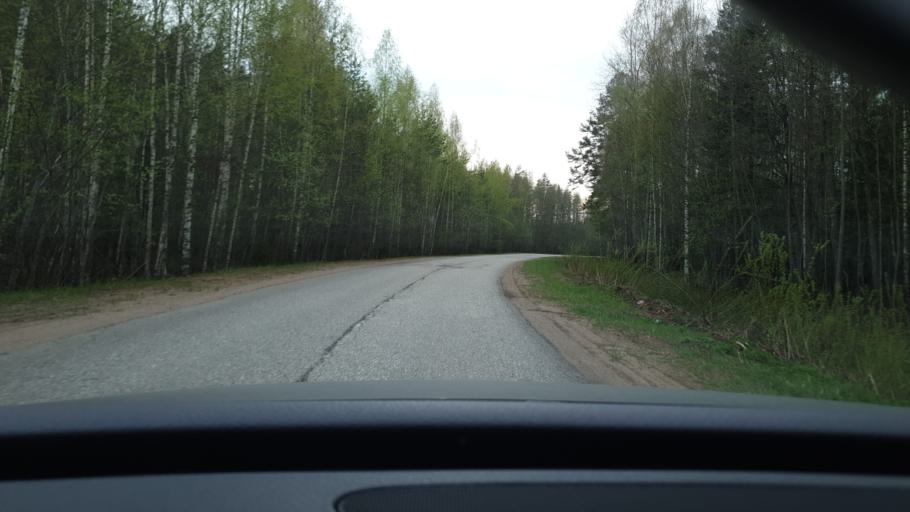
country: RU
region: Tverskaya
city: Bologoye
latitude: 57.9782
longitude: 34.0531
